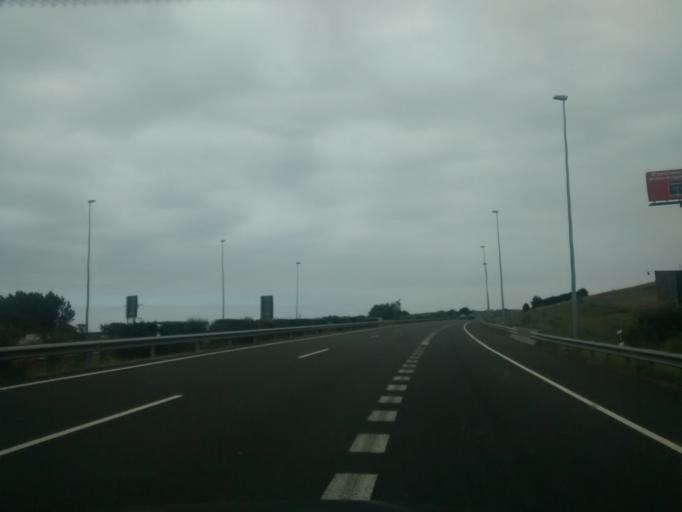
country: ES
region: Cantabria
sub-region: Provincia de Cantabria
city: Santa Cruz de Bezana
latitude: 43.4438
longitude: -3.8900
